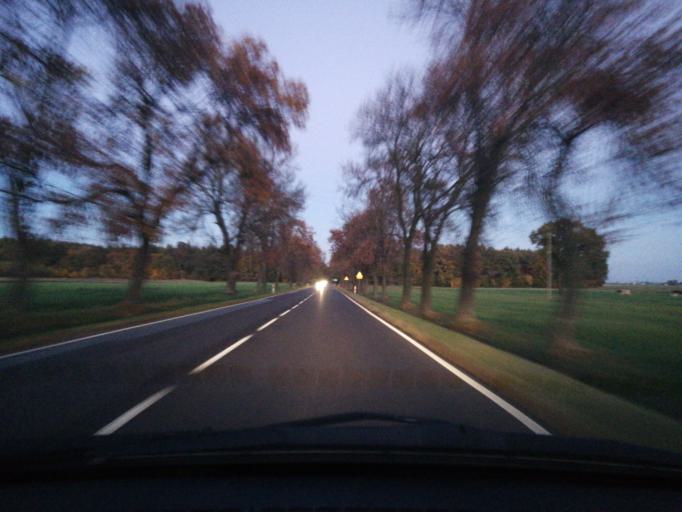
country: PL
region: Lodz Voivodeship
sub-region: Powiat brzezinski
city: Rogow
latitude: 51.8070
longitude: 19.8979
